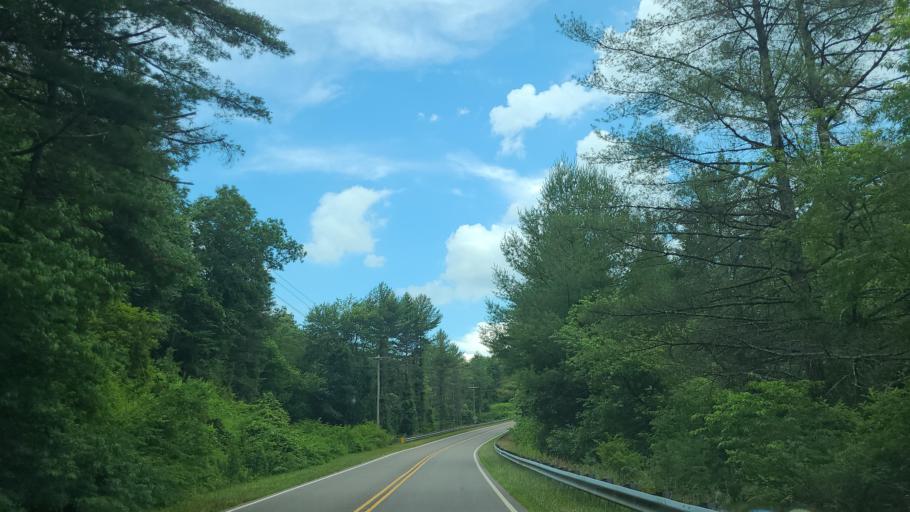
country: US
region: North Carolina
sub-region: Alleghany County
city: Sparta
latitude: 36.4092
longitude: -81.2633
